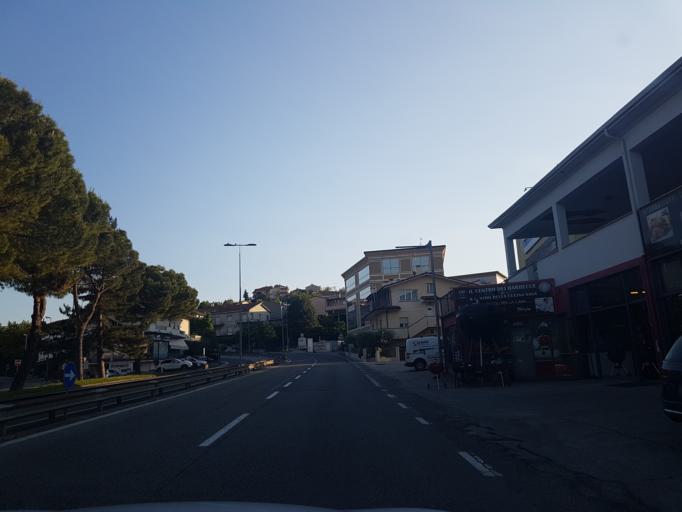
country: SM
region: Serravalle
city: Serravalle
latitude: 43.9730
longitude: 12.4835
